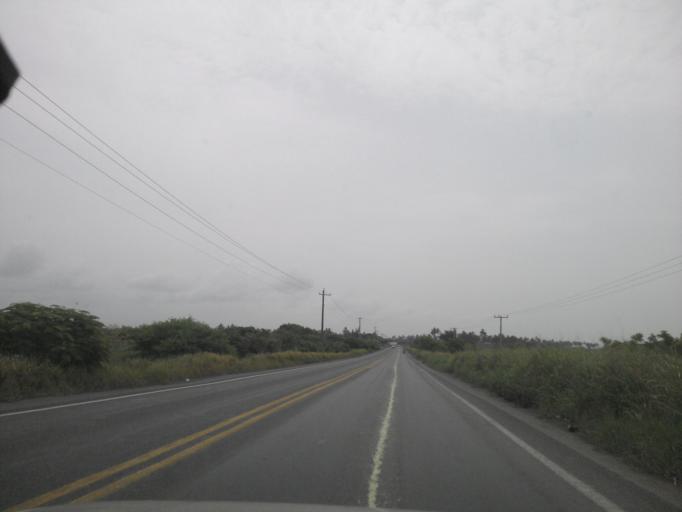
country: MX
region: Veracruz
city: Tecolutla
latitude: 20.3766
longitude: -96.9230
